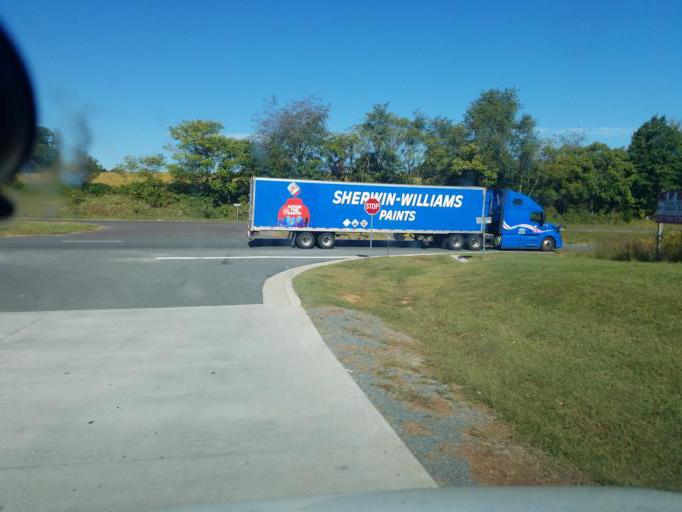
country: US
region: Virginia
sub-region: Madison County
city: Madison
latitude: 38.3554
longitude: -78.2766
